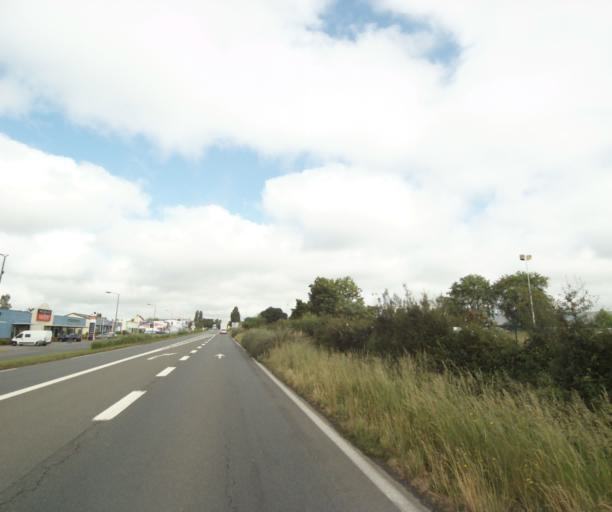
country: FR
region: Pays de la Loire
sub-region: Departement de la Sarthe
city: Solesmes
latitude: 47.8251
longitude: -0.3045
